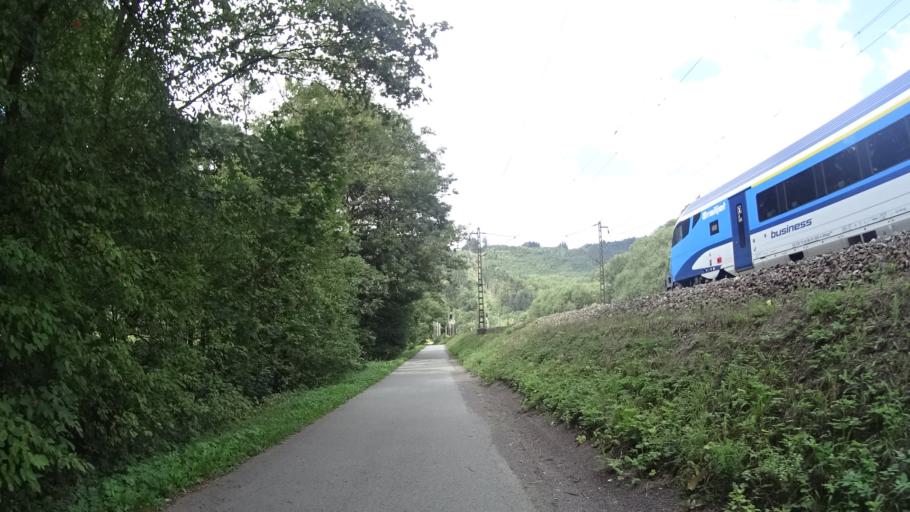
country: CZ
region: Pardubicky
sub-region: Okres Usti nad Orlici
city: Usti nad Orlici
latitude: 49.9740
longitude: 16.3431
